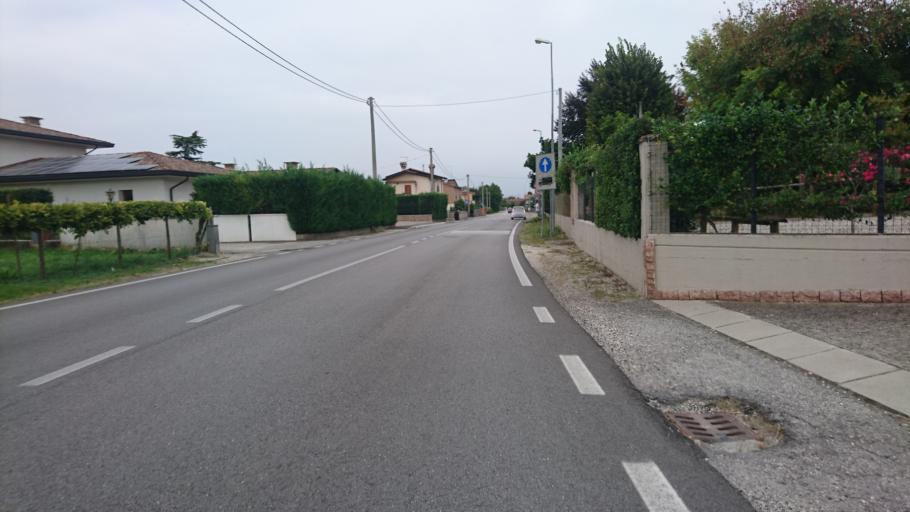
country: IT
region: Veneto
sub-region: Provincia di Padova
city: Pieve
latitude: 45.5374
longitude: 11.8349
